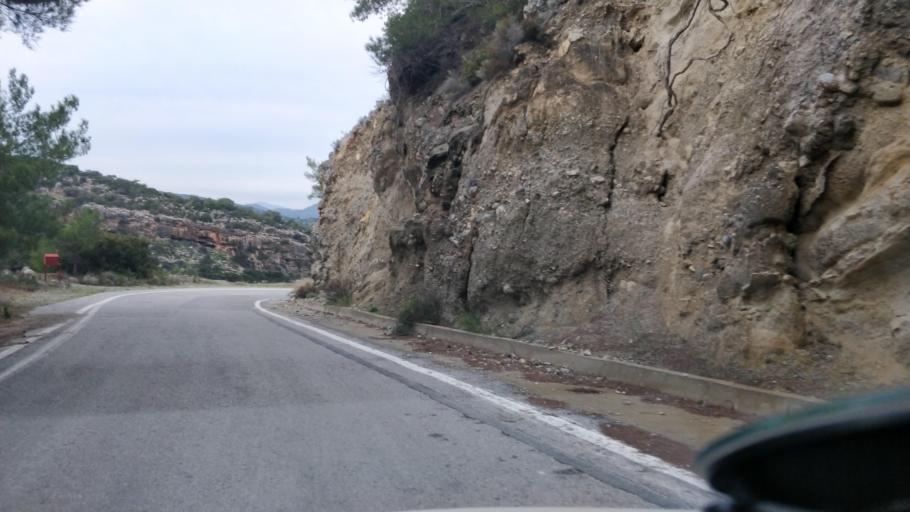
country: GR
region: Crete
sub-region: Nomos Lasithiou
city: Kritsa
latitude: 35.1036
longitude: 25.7022
